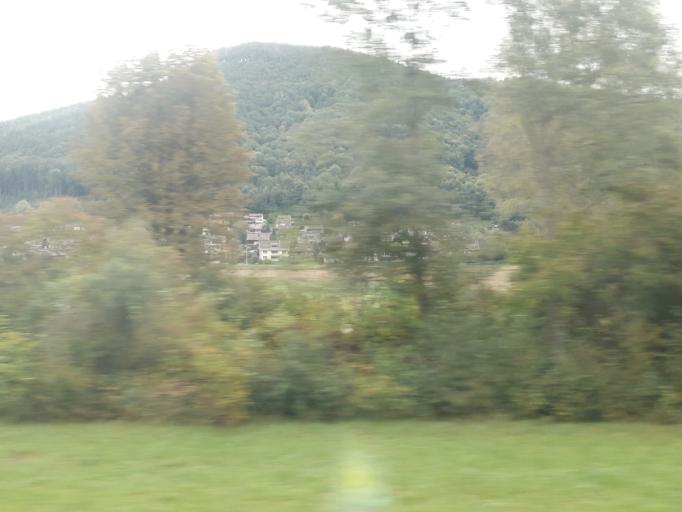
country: CH
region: Bern
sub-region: Bern-Mittelland District
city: Belp
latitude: 46.8785
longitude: 7.4993
